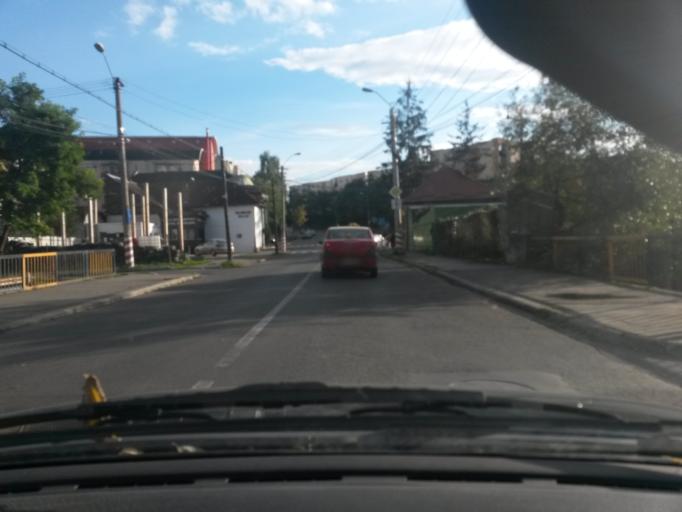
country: RO
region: Mures
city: Targu-Mures
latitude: 46.5359
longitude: 24.5657
